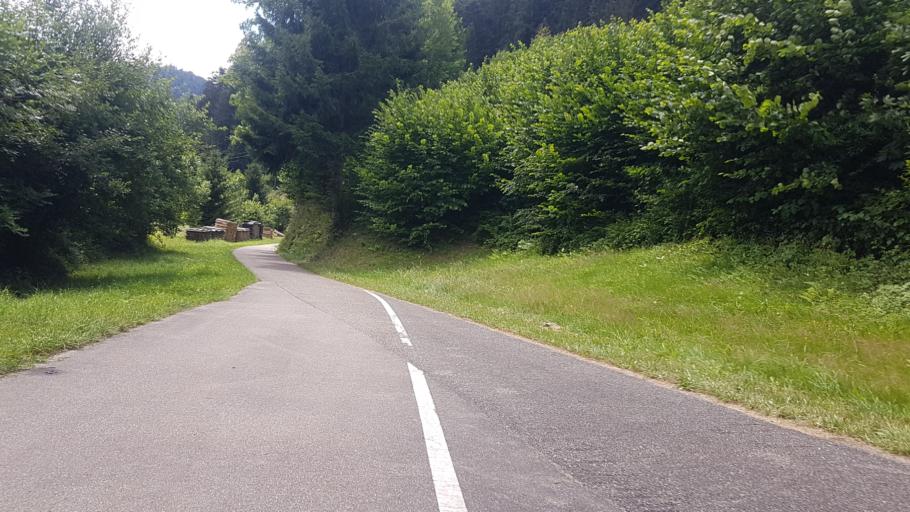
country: DE
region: Baden-Wuerttemberg
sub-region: Freiburg Region
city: Schiltach
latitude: 48.2814
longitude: 8.3513
